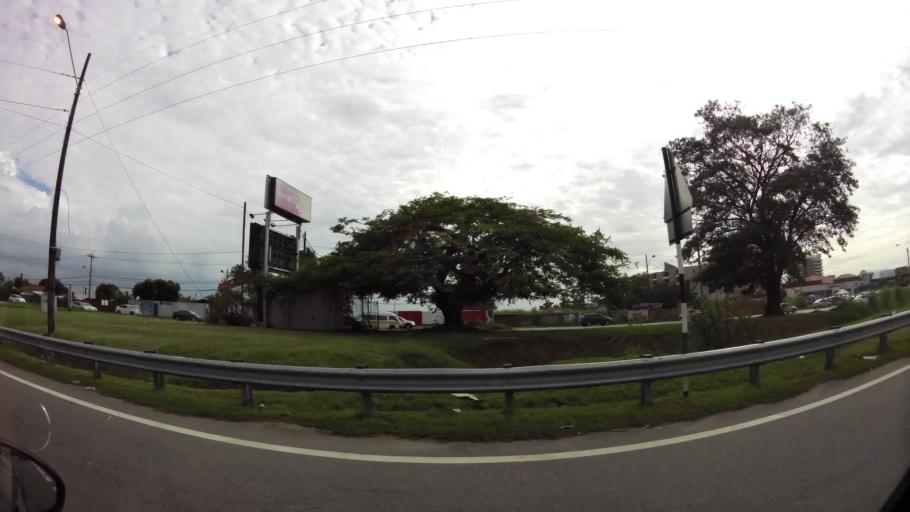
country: TT
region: City of Port of Spain
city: Mucurapo
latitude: 10.6789
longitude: -61.5503
